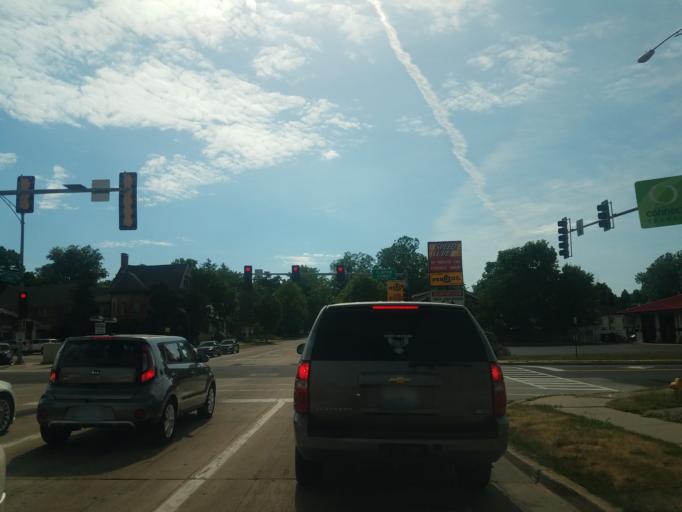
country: US
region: Illinois
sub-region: McLean County
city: Bloomington
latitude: 40.4798
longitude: -88.9843
